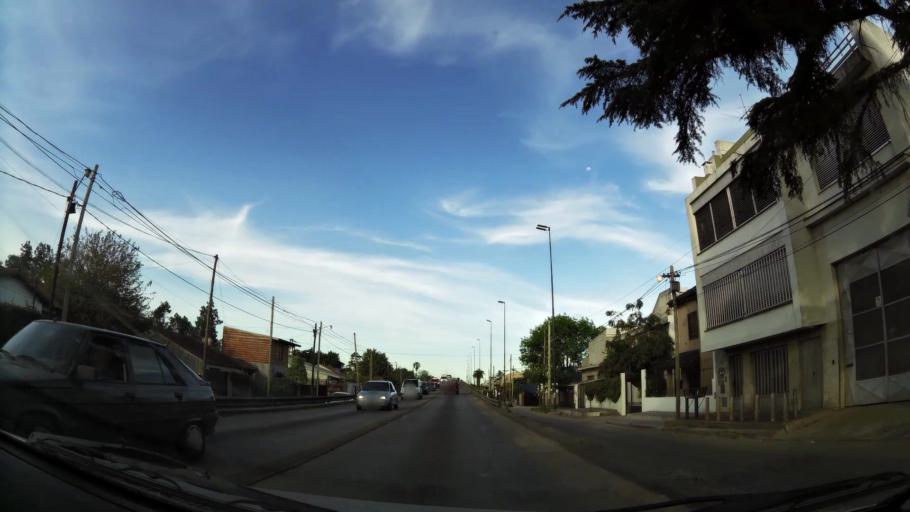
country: AR
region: Buenos Aires
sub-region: Partido de Almirante Brown
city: Adrogue
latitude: -34.8045
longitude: -58.3355
